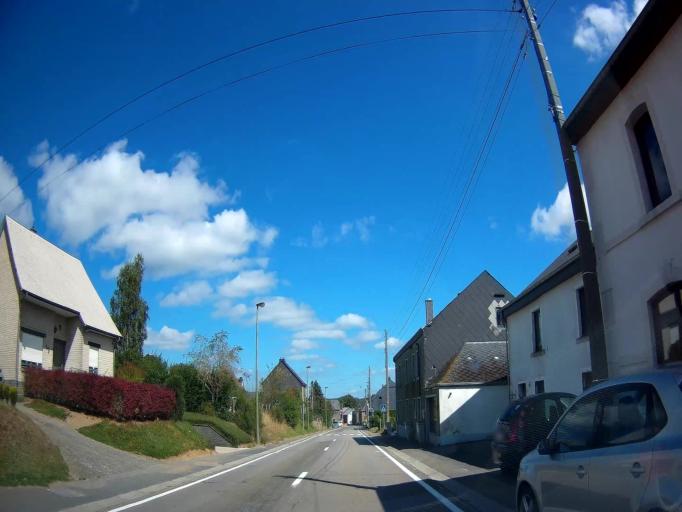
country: BE
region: Wallonia
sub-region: Province du Luxembourg
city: Bertogne
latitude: 50.0814
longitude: 5.6653
